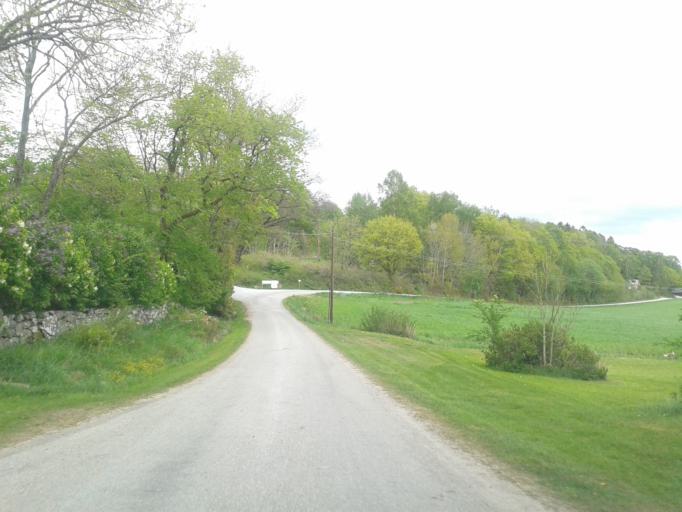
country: SE
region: Vaestra Goetaland
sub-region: Kungalvs Kommun
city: Kode
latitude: 57.8916
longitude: 11.8988
